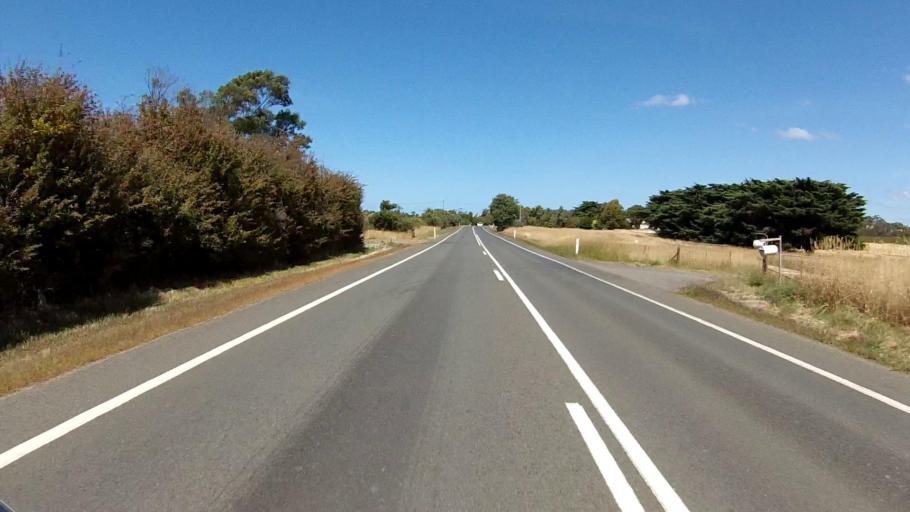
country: AU
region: Tasmania
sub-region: Break O'Day
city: St Helens
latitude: -42.0712
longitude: 148.0662
